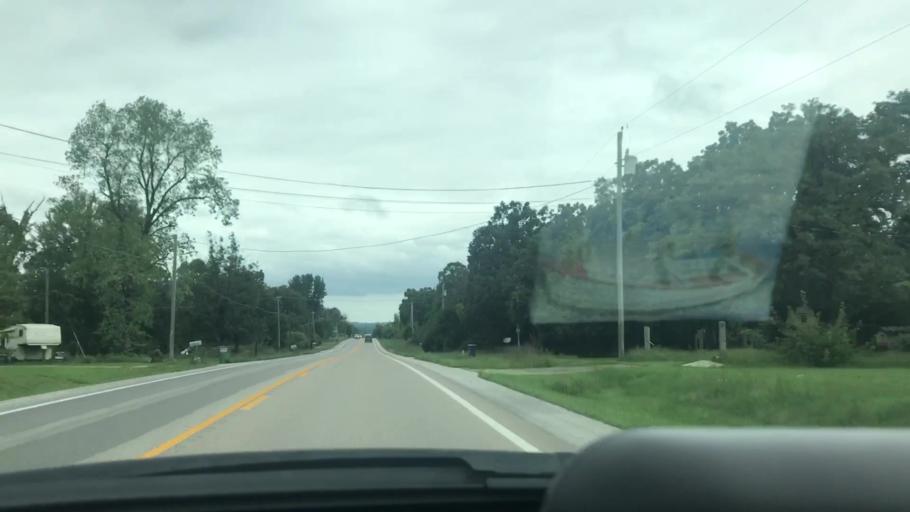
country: US
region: Missouri
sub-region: Dallas County
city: Buffalo
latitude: 37.7031
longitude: -93.1089
